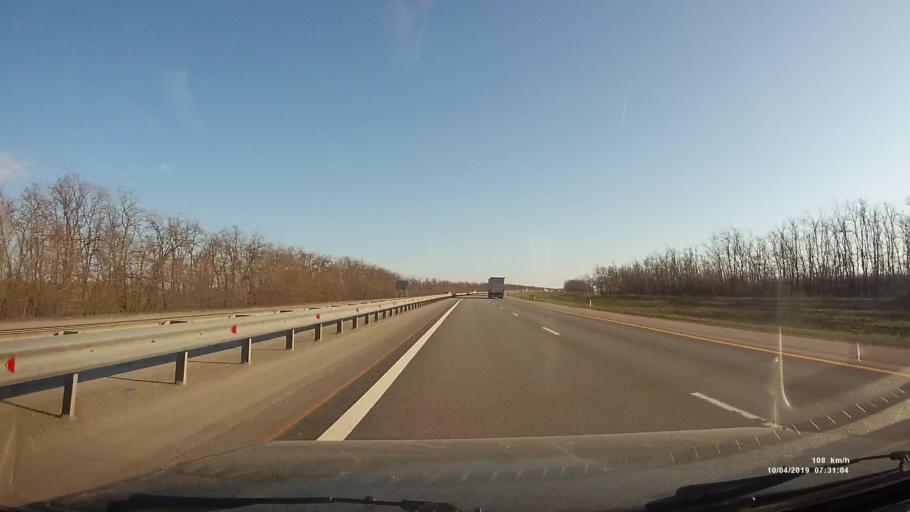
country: RU
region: Rostov
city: Zverevo
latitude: 47.9791
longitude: 40.2184
